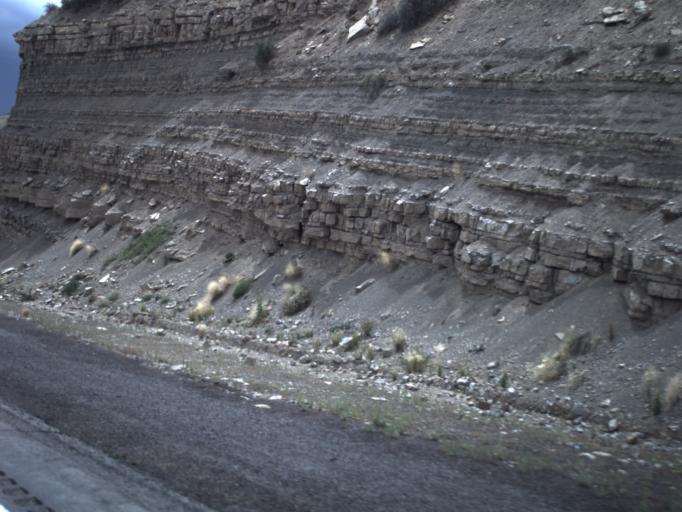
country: US
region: Utah
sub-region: Carbon County
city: Helper
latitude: 39.8155
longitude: -110.9388
